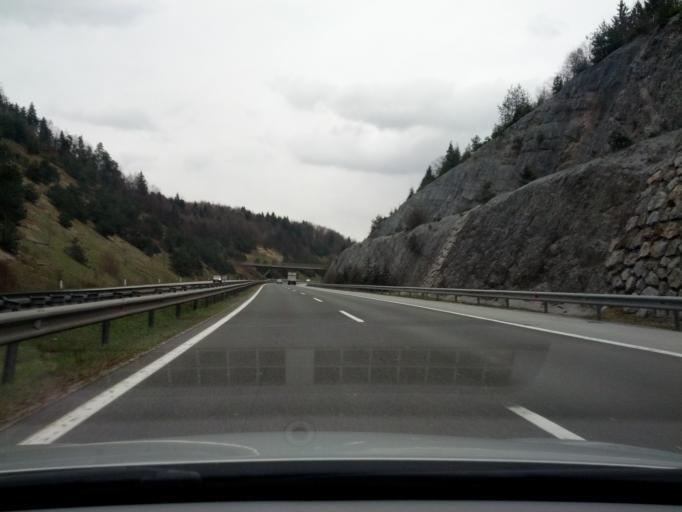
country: SI
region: Skofljica
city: Skofljica
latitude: 45.9971
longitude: 14.5867
